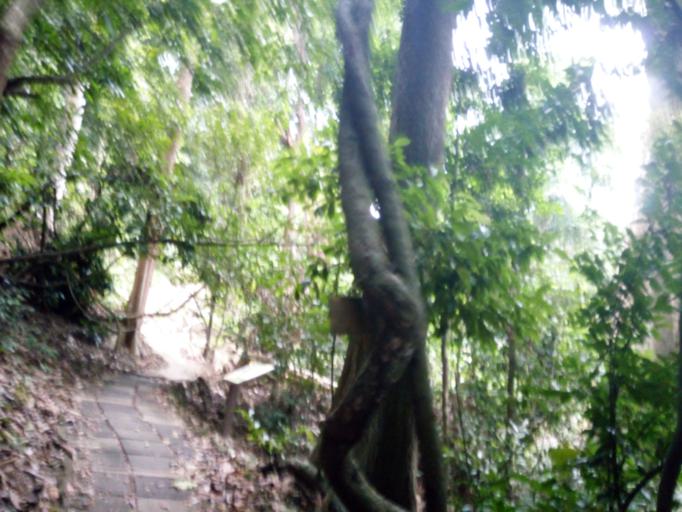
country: TH
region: Krabi
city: Ko Lanta
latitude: 7.4738
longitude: 99.0960
